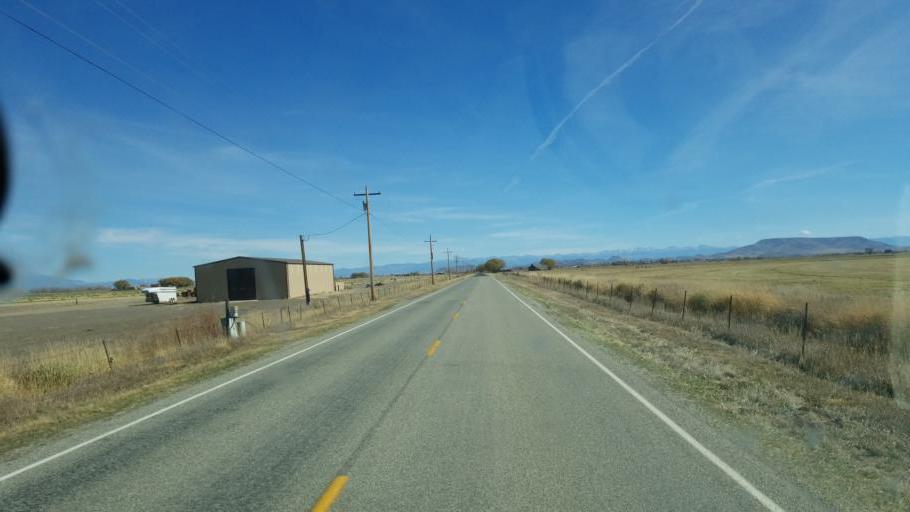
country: US
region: Colorado
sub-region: Conejos County
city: Conejos
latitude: 37.2836
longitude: -106.0151
